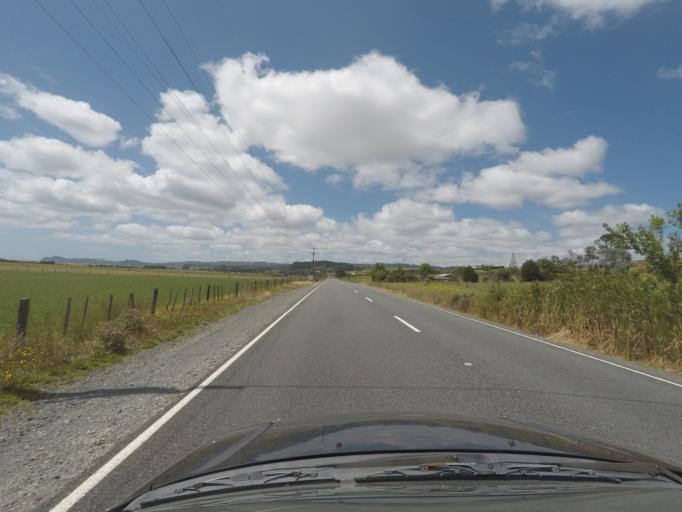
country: NZ
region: Northland
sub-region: Whangarei
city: Ruakaka
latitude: -36.0067
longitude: 174.4792
